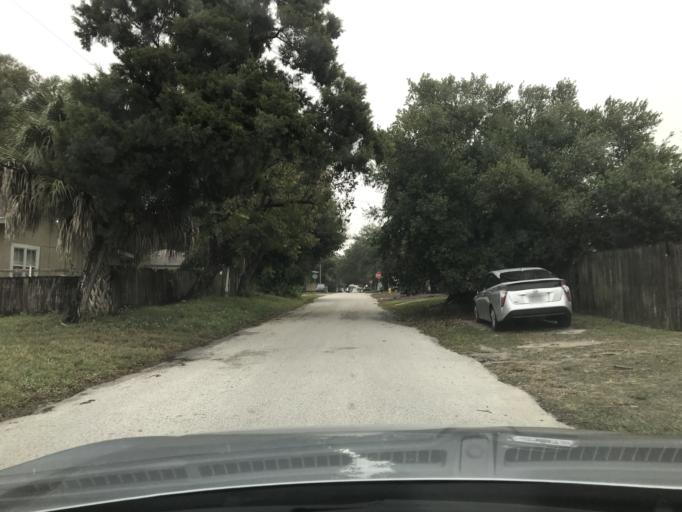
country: US
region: Florida
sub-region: Hillsborough County
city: Tampa
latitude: 27.9790
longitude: -82.4628
